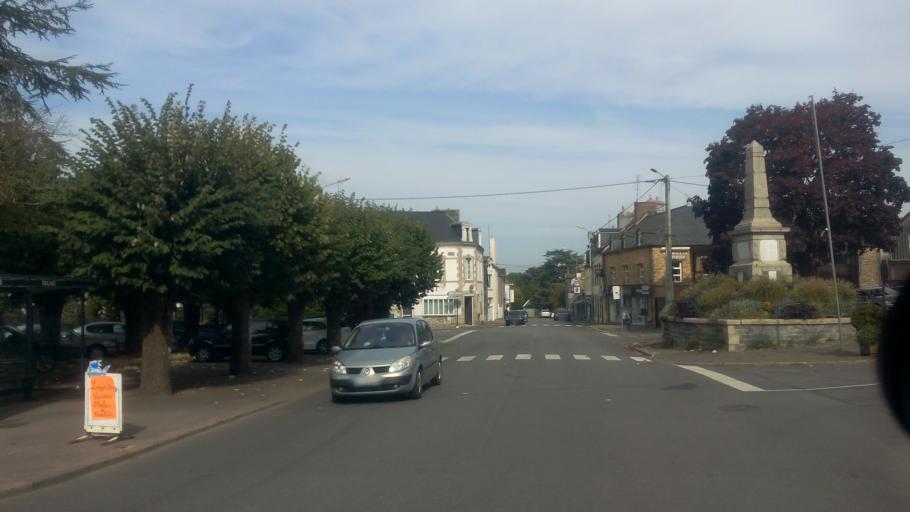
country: FR
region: Brittany
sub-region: Departement du Morbihan
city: La Gacilly
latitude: 47.7652
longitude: -2.1312
